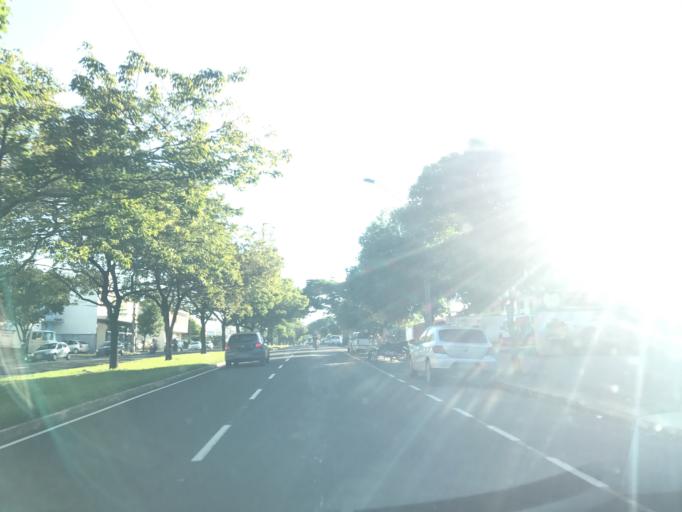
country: BR
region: Parana
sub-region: Maringa
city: Maringa
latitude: -23.4487
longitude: -51.9493
